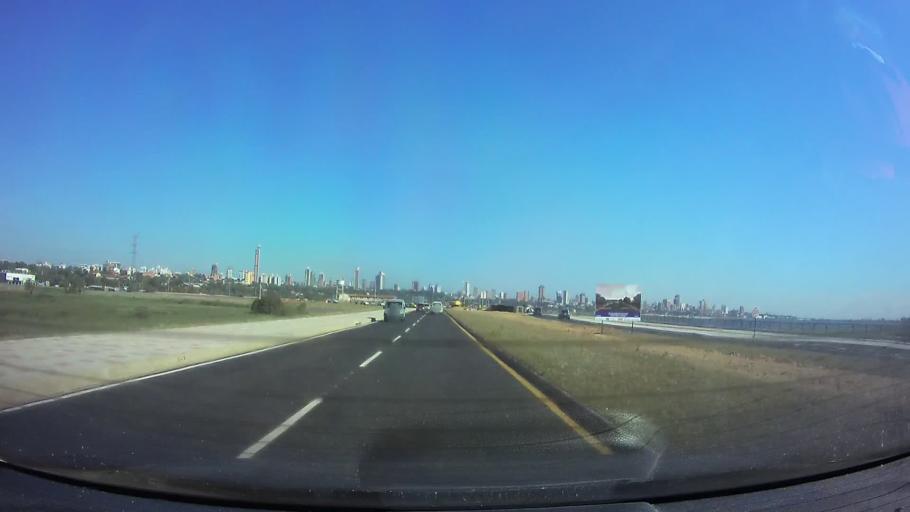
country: PY
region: Asuncion
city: Asuncion
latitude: -25.2683
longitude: -57.6116
